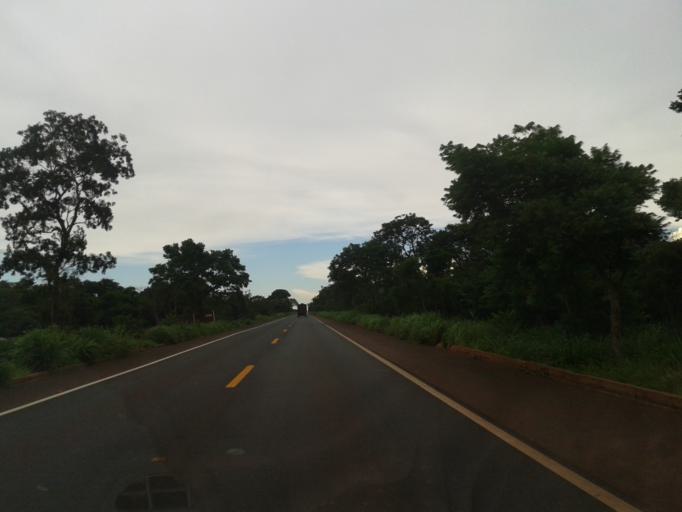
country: BR
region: Minas Gerais
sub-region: Santa Vitoria
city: Santa Vitoria
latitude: -18.8893
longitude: -50.1590
